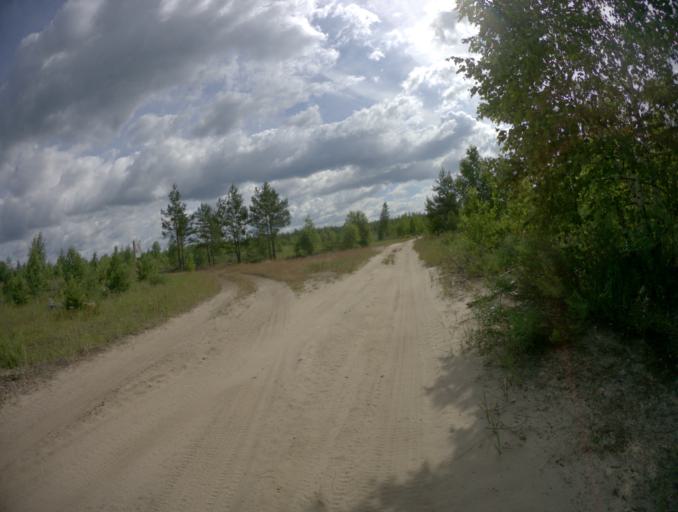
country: RU
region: Ivanovo
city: Talitsy
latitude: 56.5366
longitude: 42.4491
